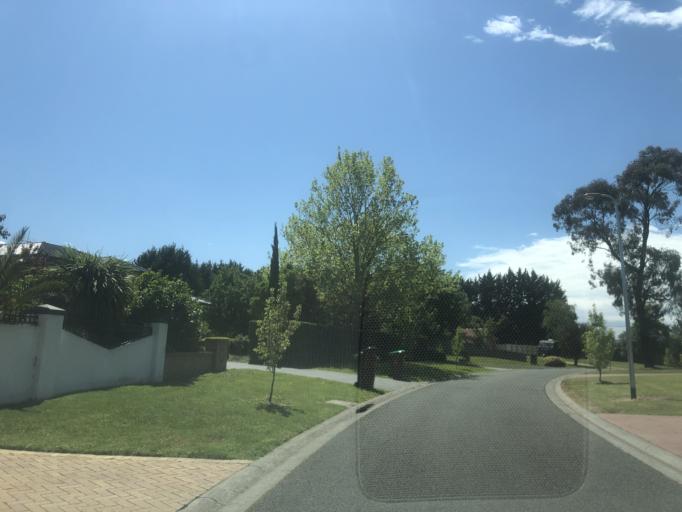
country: AU
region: Victoria
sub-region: Casey
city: Endeavour Hills
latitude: -37.9802
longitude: 145.2855
